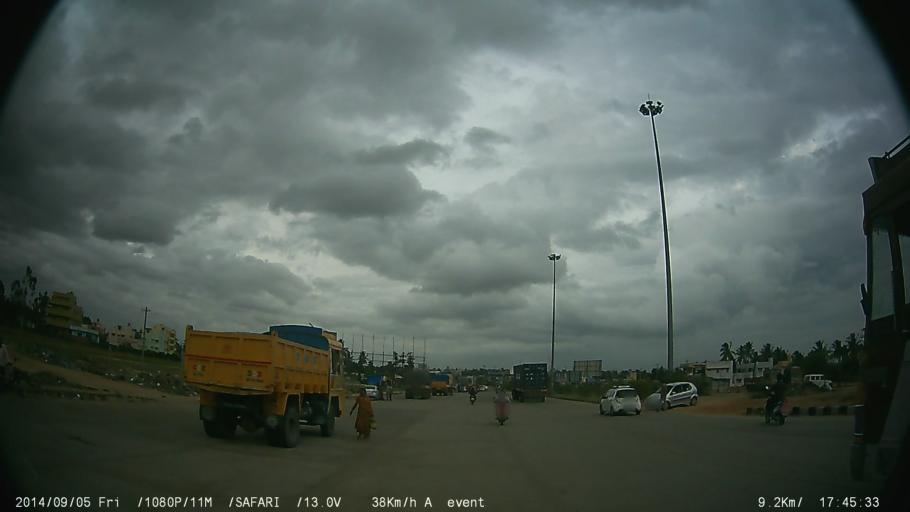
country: IN
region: Tamil Nadu
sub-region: Krishnagiri
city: Hosur
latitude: 12.7767
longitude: 77.7779
